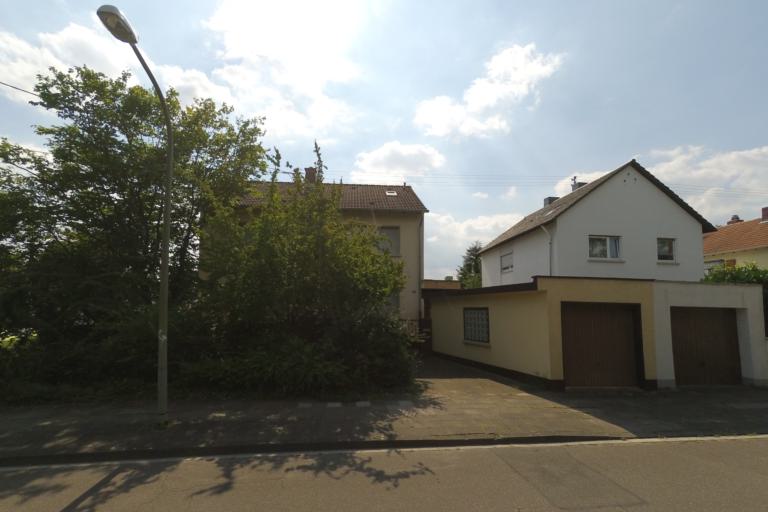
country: DE
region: Rheinland-Pfalz
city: Frankenthal
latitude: 49.4937
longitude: 8.3655
